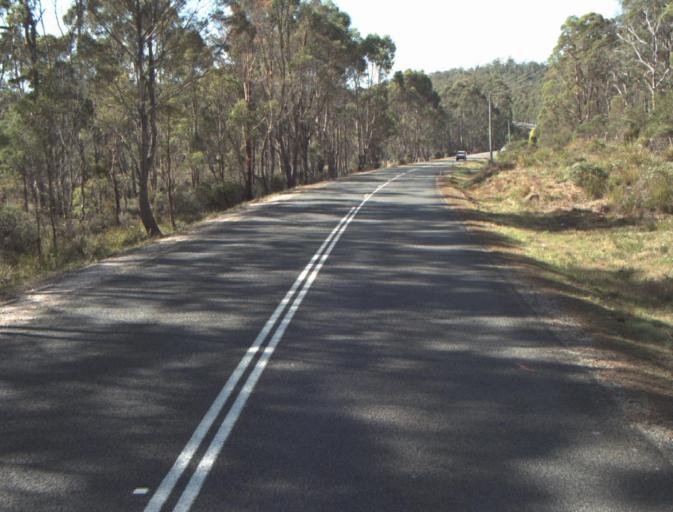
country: AU
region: Tasmania
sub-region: Launceston
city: Mayfield
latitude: -41.3286
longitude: 147.1815
